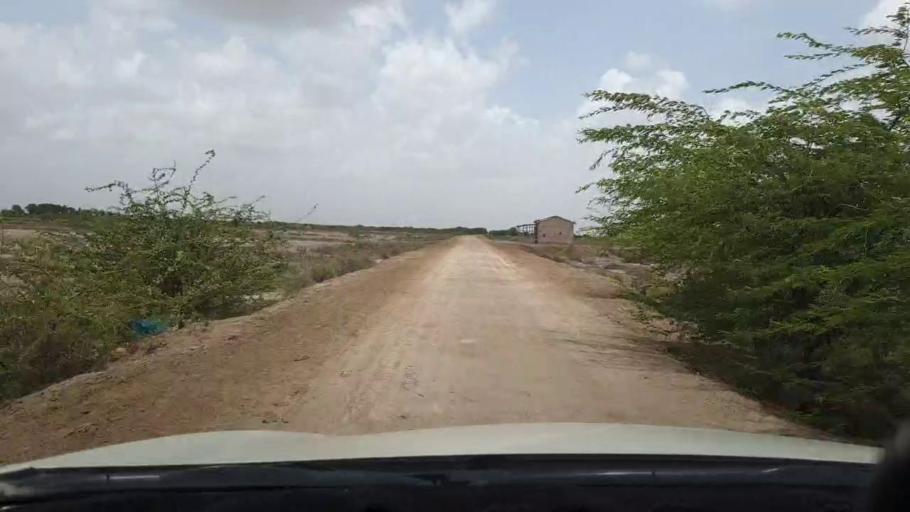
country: PK
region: Sindh
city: Kadhan
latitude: 24.3603
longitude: 68.9383
